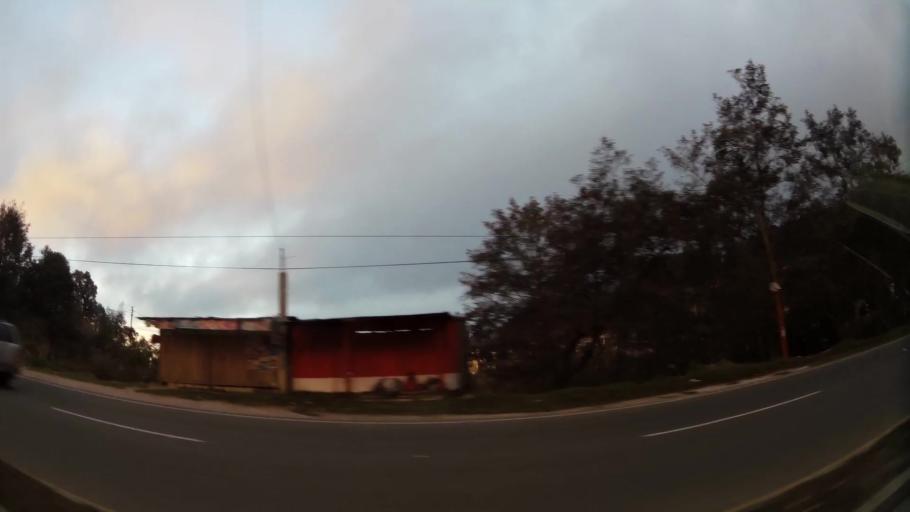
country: GT
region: Solola
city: Concepcion
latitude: 14.8490
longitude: -91.1458
